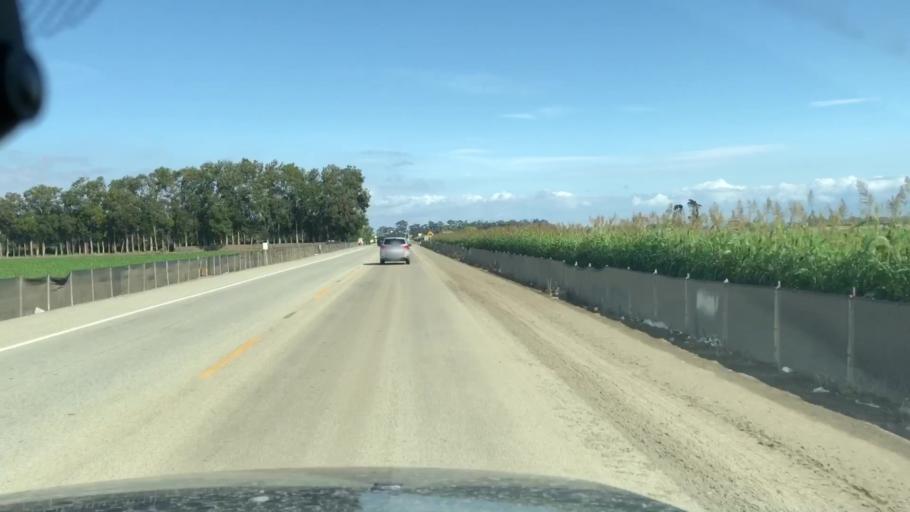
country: US
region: California
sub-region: Ventura County
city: Oxnard Shores
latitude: 34.2442
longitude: -119.2407
